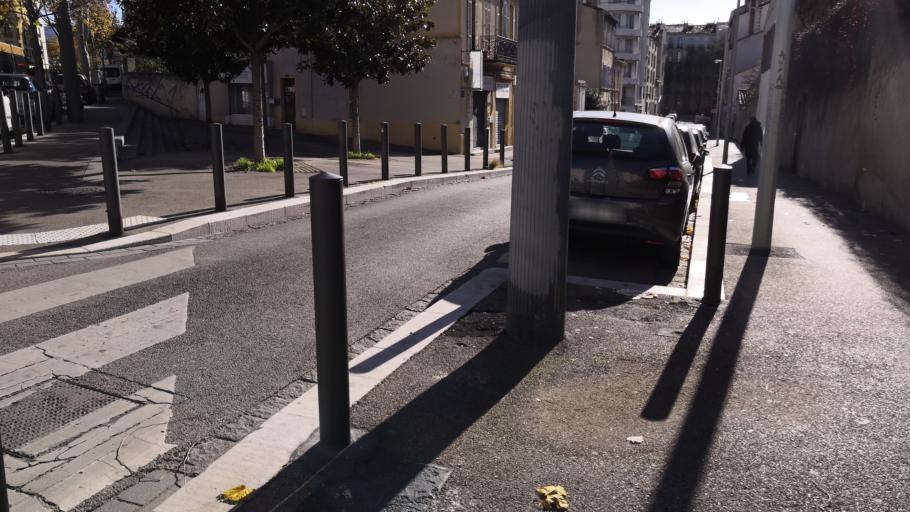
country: FR
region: Provence-Alpes-Cote d'Azur
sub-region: Departement des Bouches-du-Rhone
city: Marseille 05
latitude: 43.2976
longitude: 5.4038
